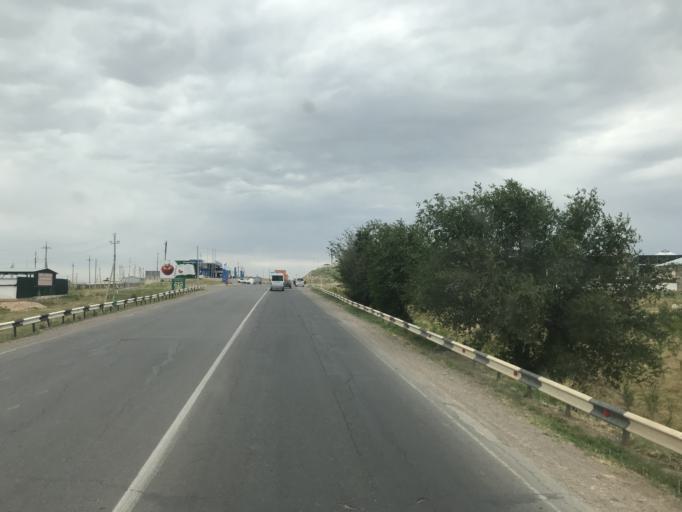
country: KZ
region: Ongtustik Qazaqstan
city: Saryaghash
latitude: 41.4739
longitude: 69.1990
